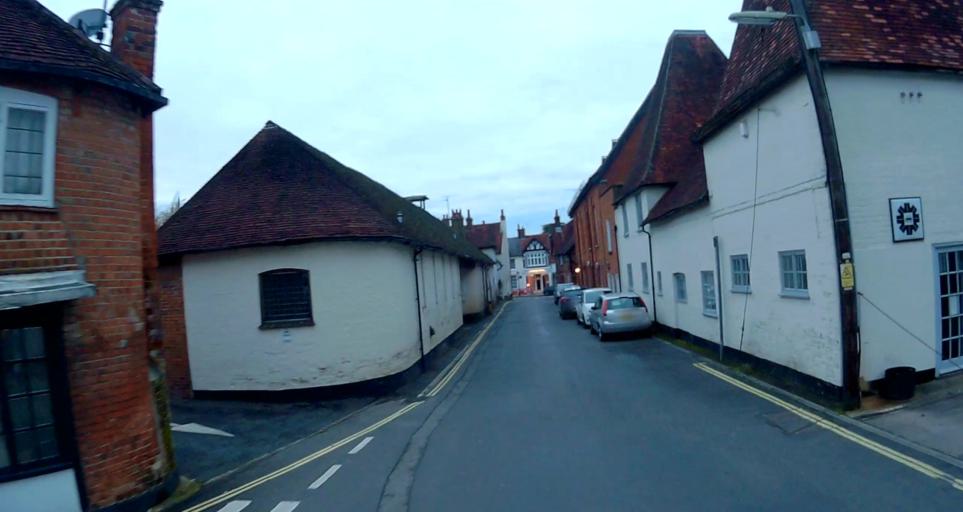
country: GB
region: England
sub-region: Hampshire
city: Odiham
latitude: 51.2534
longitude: -0.9391
